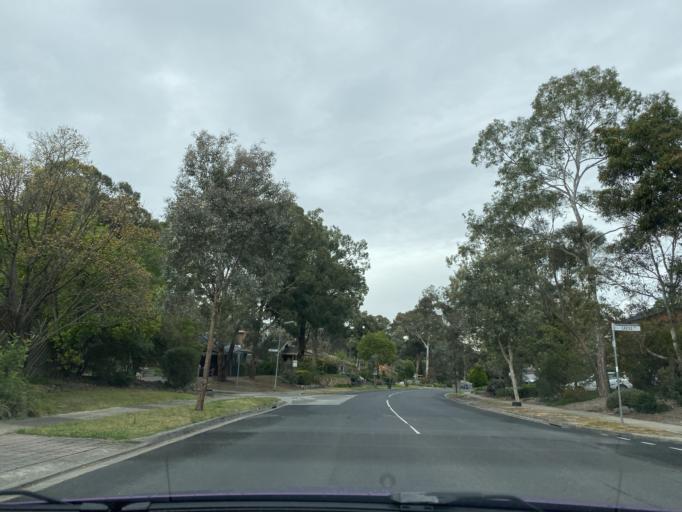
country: AU
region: Victoria
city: Saint Helena
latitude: -37.6908
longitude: 145.1368
